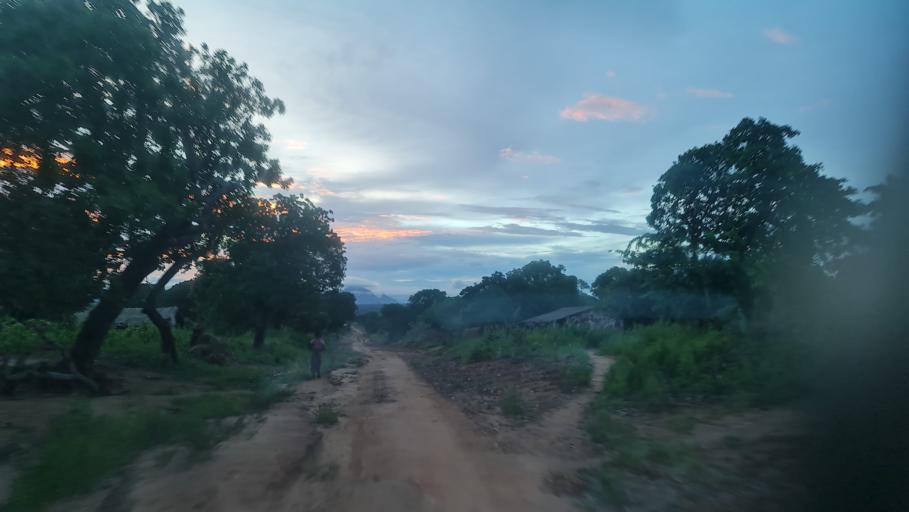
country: MZ
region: Nampula
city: Nampula
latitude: -14.7344
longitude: 39.9186
